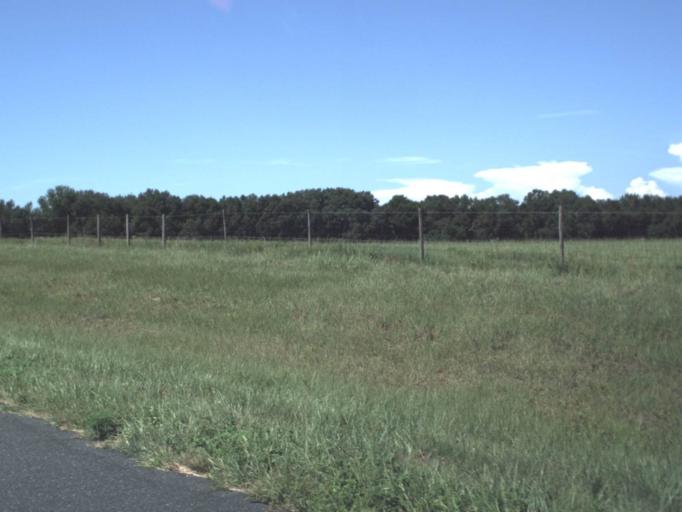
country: US
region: Florida
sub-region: Levy County
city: Williston Highlands
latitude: 29.2555
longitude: -82.4416
